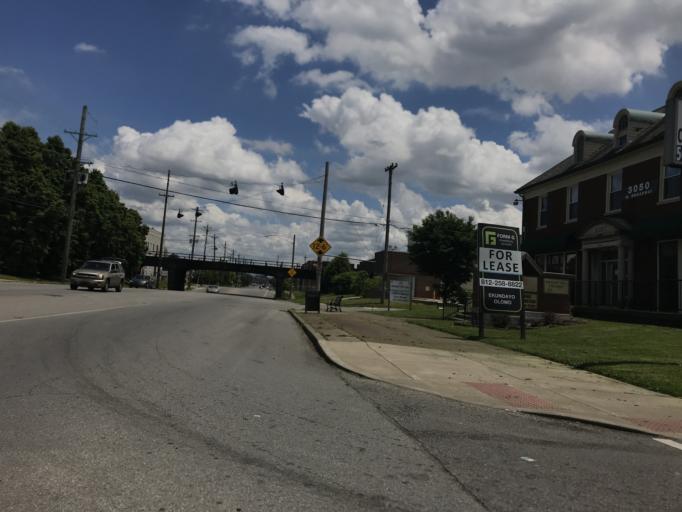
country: US
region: Indiana
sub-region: Floyd County
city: New Albany
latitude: 38.2497
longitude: -85.8038
